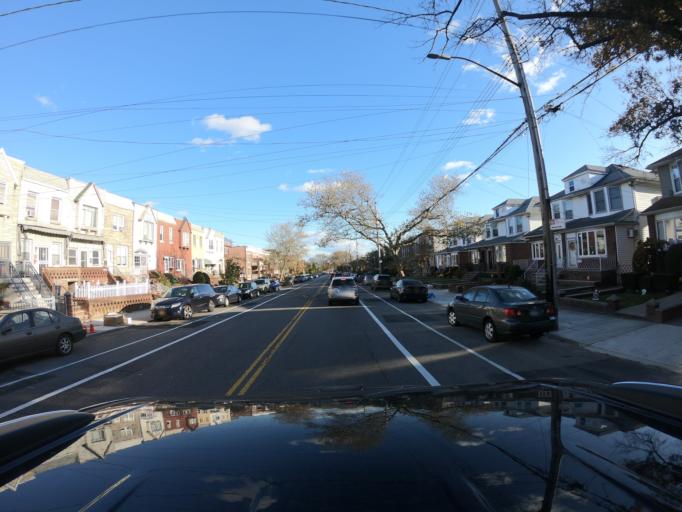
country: US
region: New York
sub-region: Kings County
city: Bensonhurst
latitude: 40.6225
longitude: -74.0112
